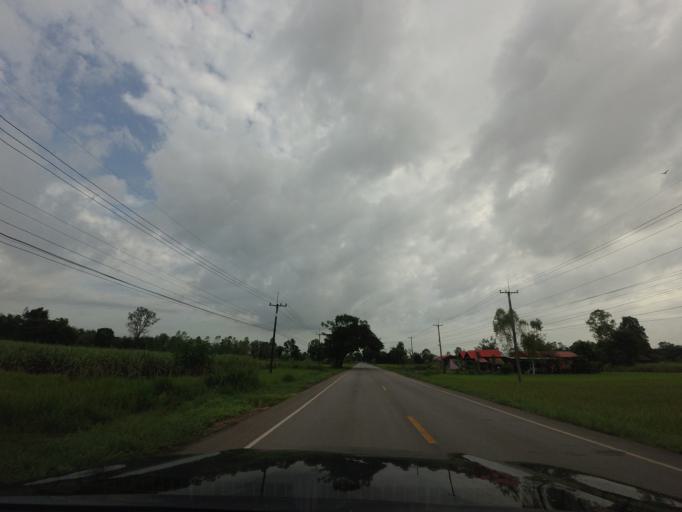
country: TH
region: Changwat Udon Thani
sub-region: Amphoe Ban Phue
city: Ban Phue
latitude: 17.7316
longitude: 102.3959
